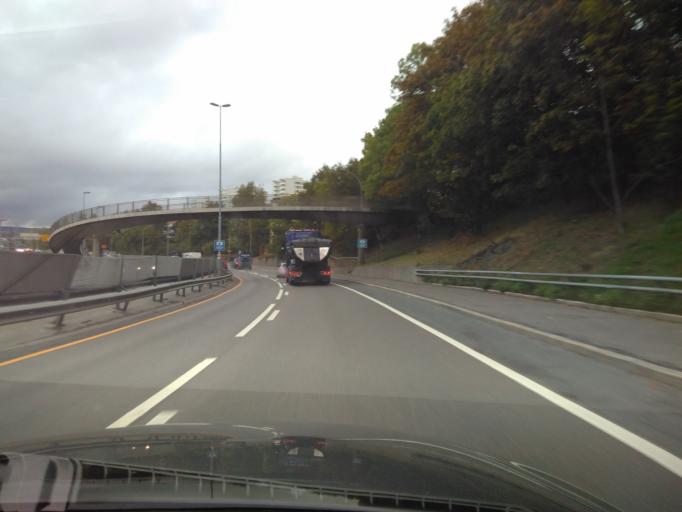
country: NO
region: Oslo
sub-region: Oslo
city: Oslo
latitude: 59.9503
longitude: 10.7771
